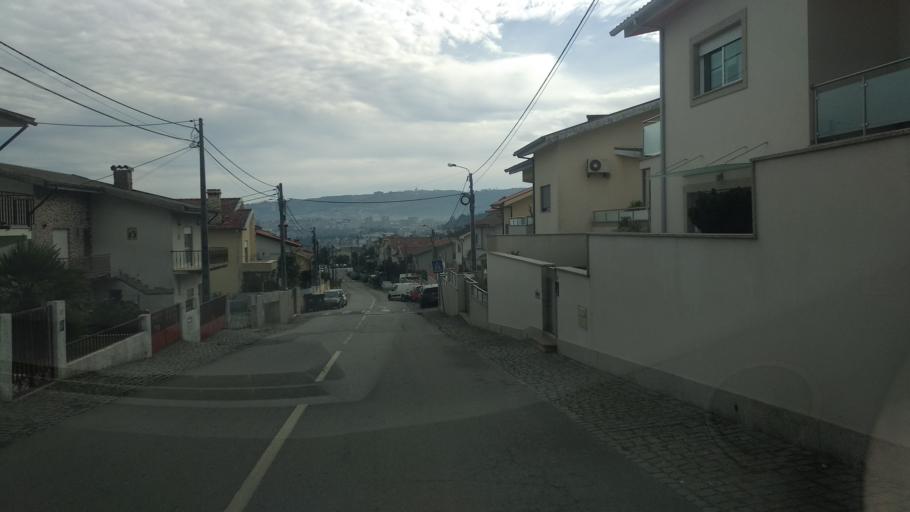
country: PT
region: Braga
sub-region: Braga
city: Braga
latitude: 41.5449
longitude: -8.4630
